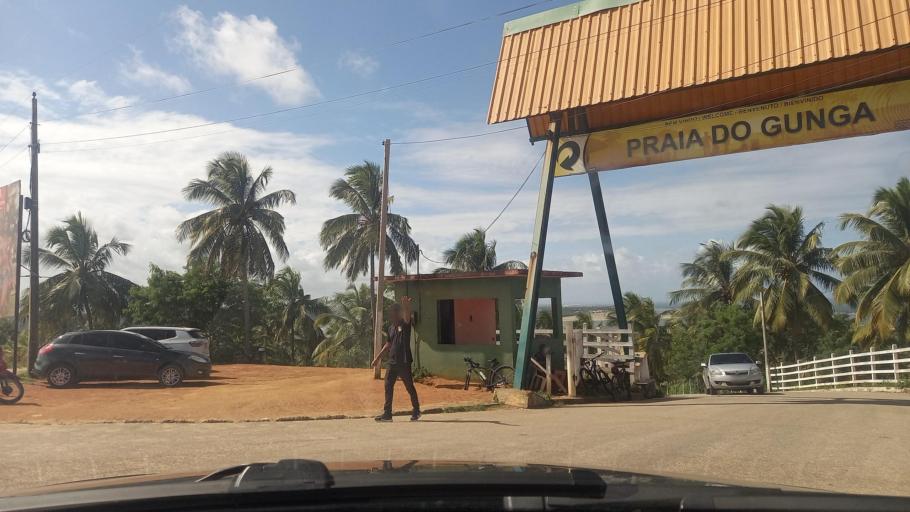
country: BR
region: Alagoas
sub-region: Marechal Deodoro
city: Marechal Deodoro
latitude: -9.8651
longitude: -35.9147
